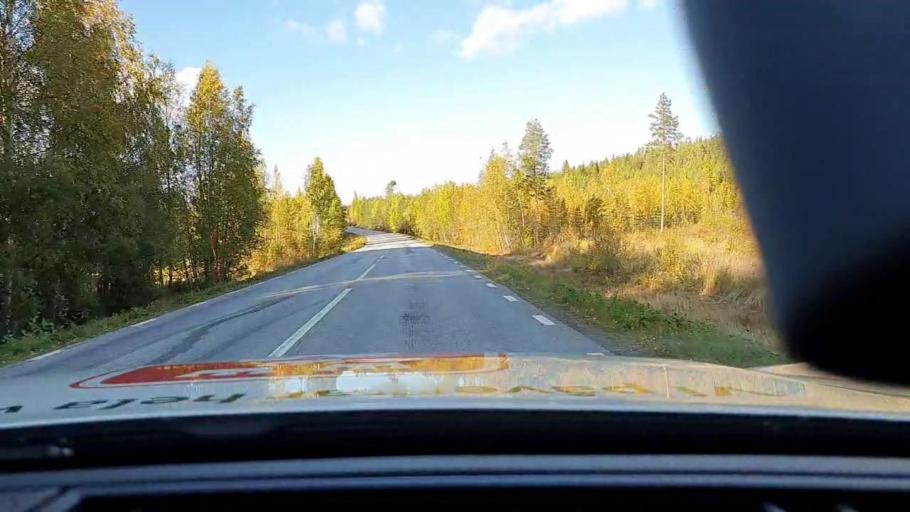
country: SE
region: Norrbotten
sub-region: Pitea Kommun
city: Norrfjarden
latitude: 65.4496
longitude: 21.4566
